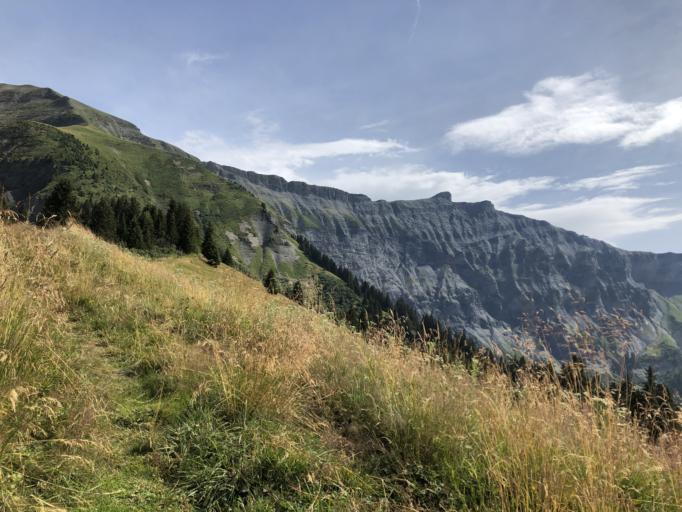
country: FR
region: Rhone-Alpes
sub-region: Departement de la Haute-Savoie
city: Megeve
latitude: 45.8227
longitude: 6.6625
